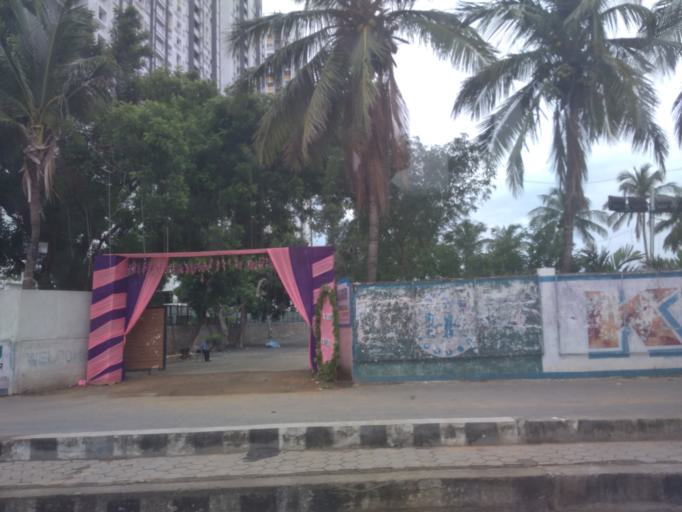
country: IN
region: Tamil Nadu
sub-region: Kancheepuram
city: Injambakkam
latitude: 12.8936
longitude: 80.2276
